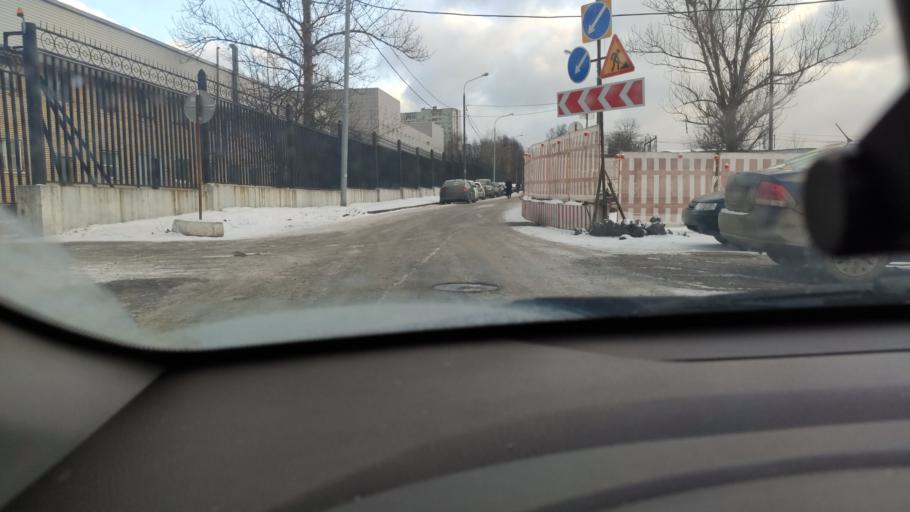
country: RU
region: Moscow
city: Tsaritsyno
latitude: 55.6161
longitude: 37.6525
